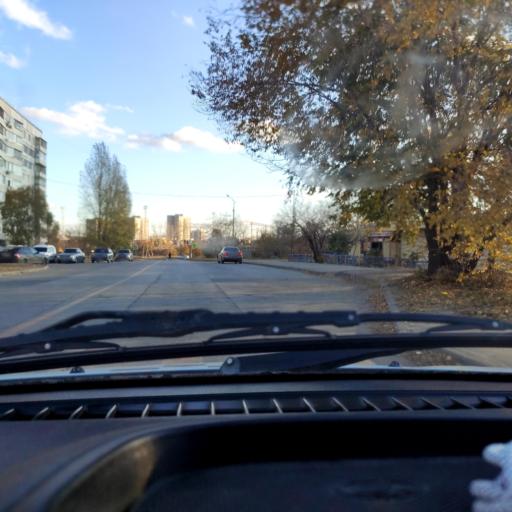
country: RU
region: Samara
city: Zhigulevsk
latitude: 53.4829
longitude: 49.5169
